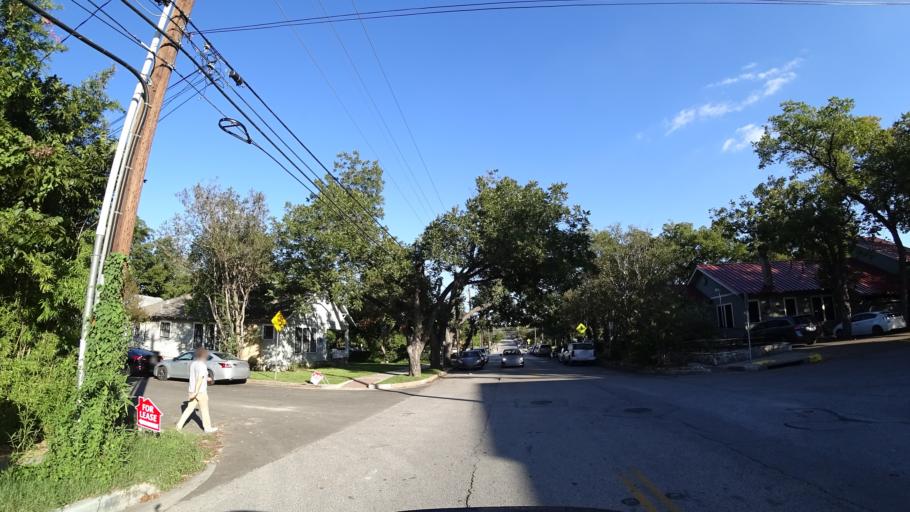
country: US
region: Texas
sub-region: Travis County
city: Austin
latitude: 30.2961
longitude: -97.7412
